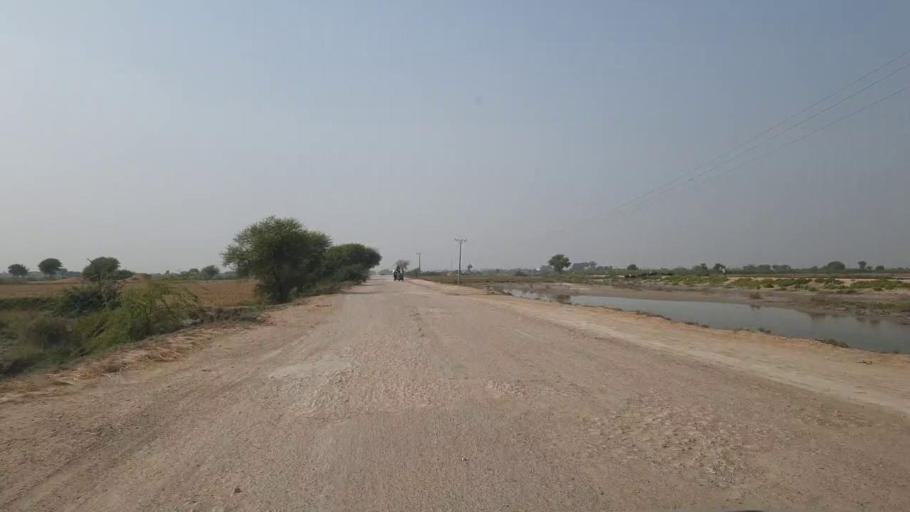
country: PK
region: Sindh
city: Matli
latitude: 25.0262
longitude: 68.6735
